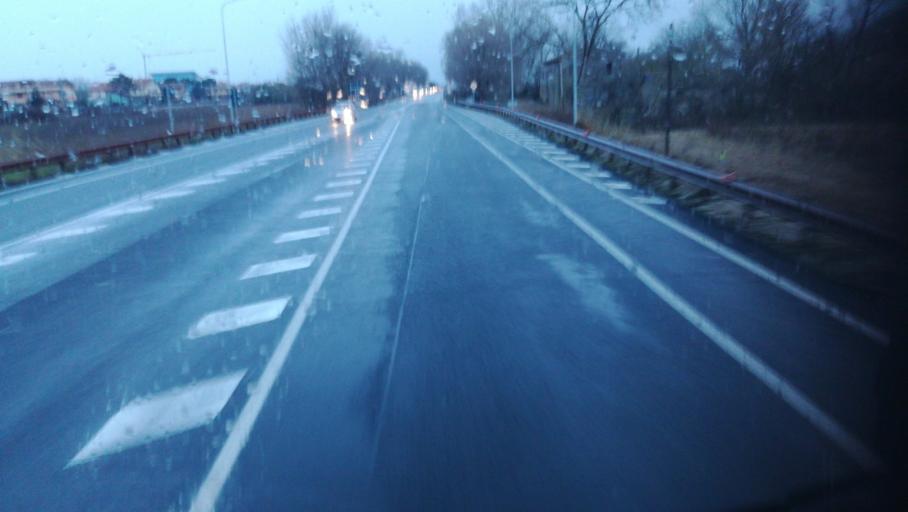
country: IT
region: Emilia-Romagna
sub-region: Provincia di Ravenna
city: Cervia
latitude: 44.2301
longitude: 12.3640
